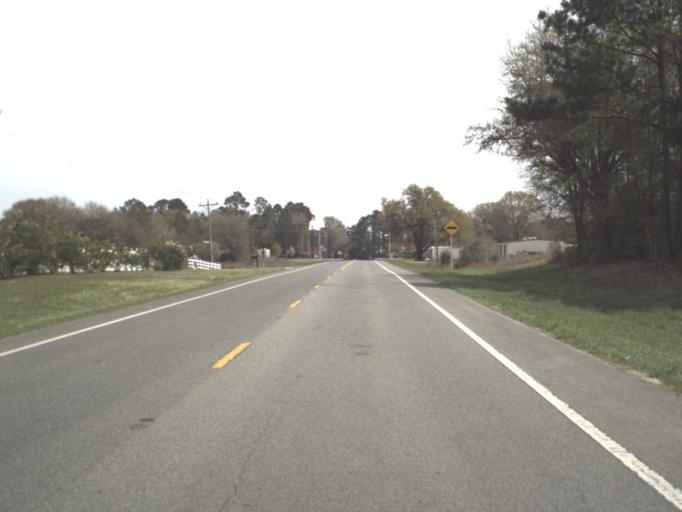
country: US
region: Alabama
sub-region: Geneva County
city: Geneva
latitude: 30.9439
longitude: -85.8233
